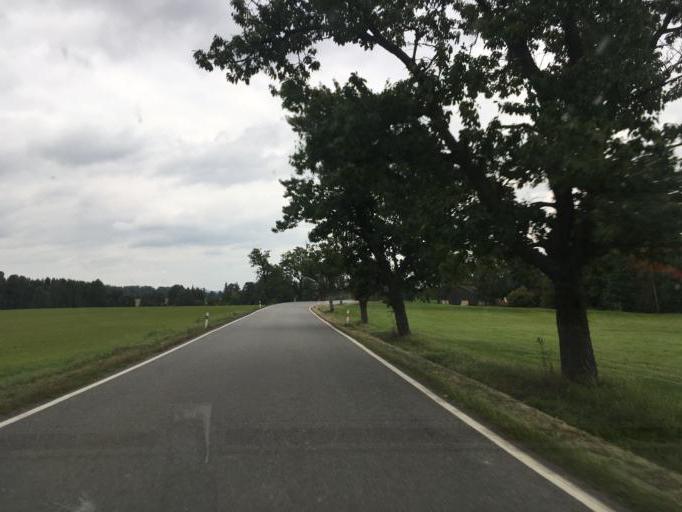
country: CZ
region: Vysocina
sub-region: Okres Jihlava
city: Telc
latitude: 49.2097
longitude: 15.4329
